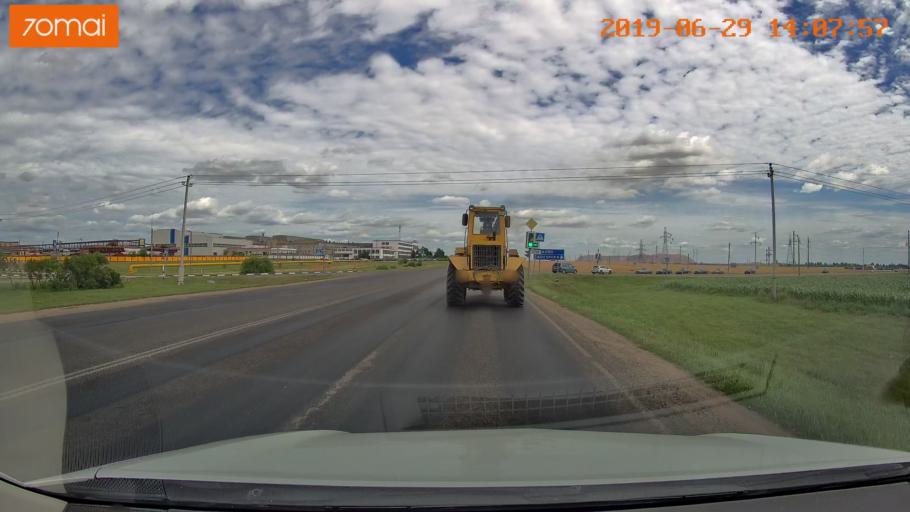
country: BY
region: Minsk
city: Salihorsk
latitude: 52.8529
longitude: 27.4725
